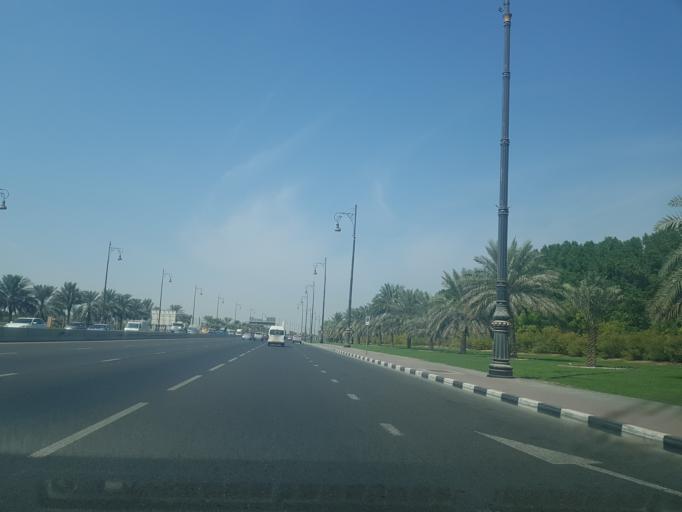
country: AE
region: Ash Shariqah
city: Sharjah
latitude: 25.3184
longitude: 55.5150
